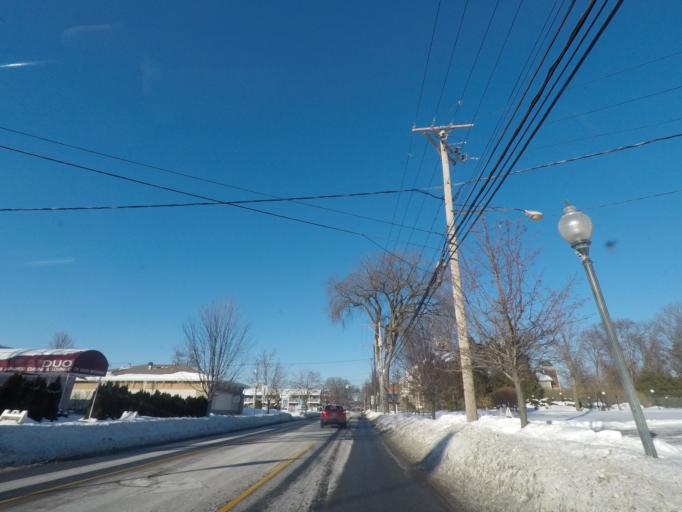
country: US
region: New York
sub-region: Saratoga County
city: Saratoga Springs
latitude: 43.0724
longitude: -73.7879
